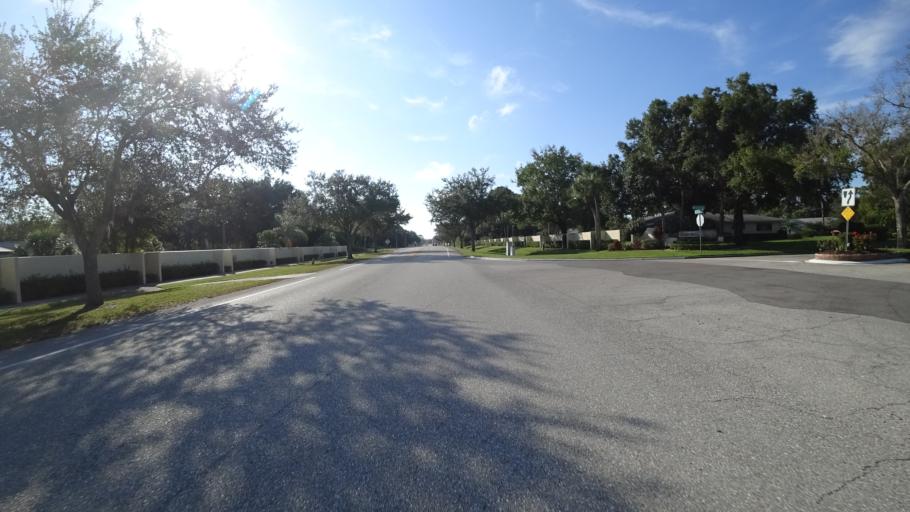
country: US
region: Florida
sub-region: Sarasota County
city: Desoto Lakes
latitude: 27.4158
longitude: -82.4914
